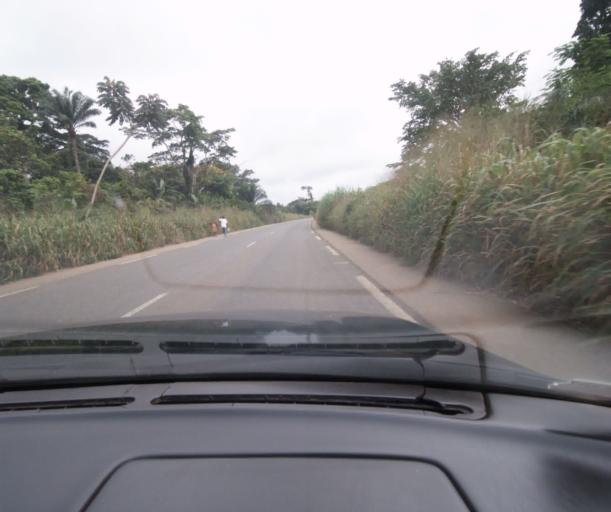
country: CM
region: Centre
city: Ombesa
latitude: 4.5980
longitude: 11.2584
